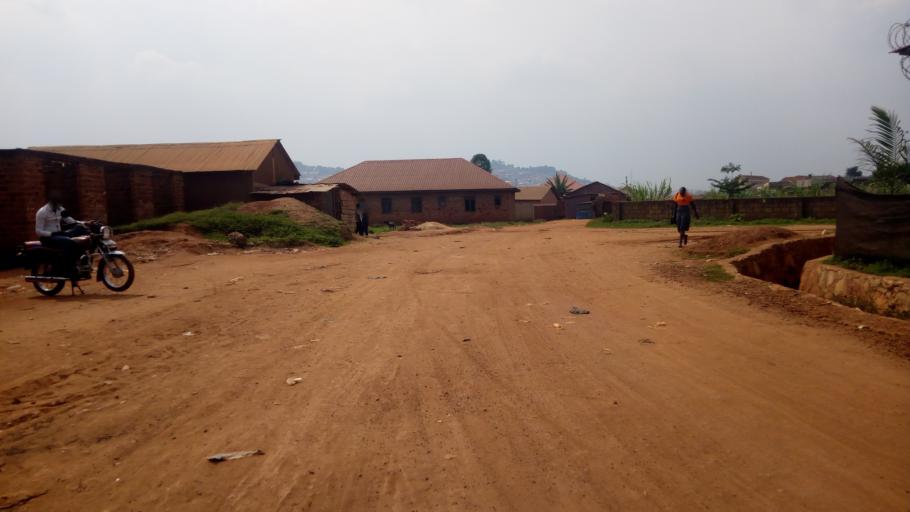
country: UG
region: Central Region
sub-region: Wakiso District
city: Kireka
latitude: 0.3192
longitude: 32.6522
